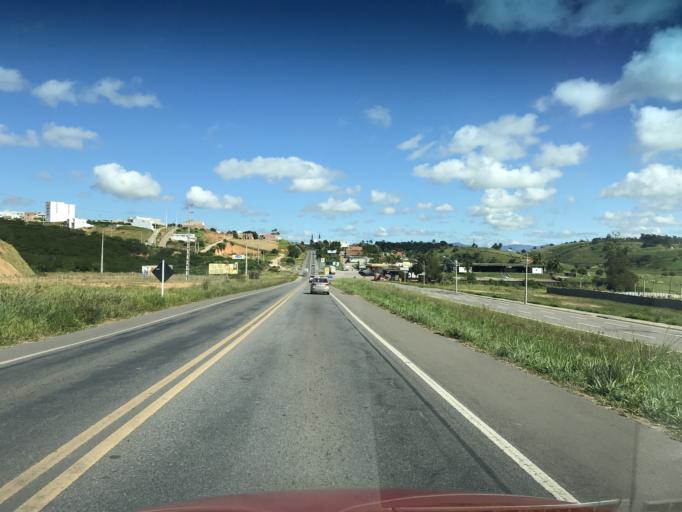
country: BR
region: Bahia
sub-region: Santo Antonio De Jesus
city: Santo Antonio de Jesus
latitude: -12.9558
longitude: -39.2611
